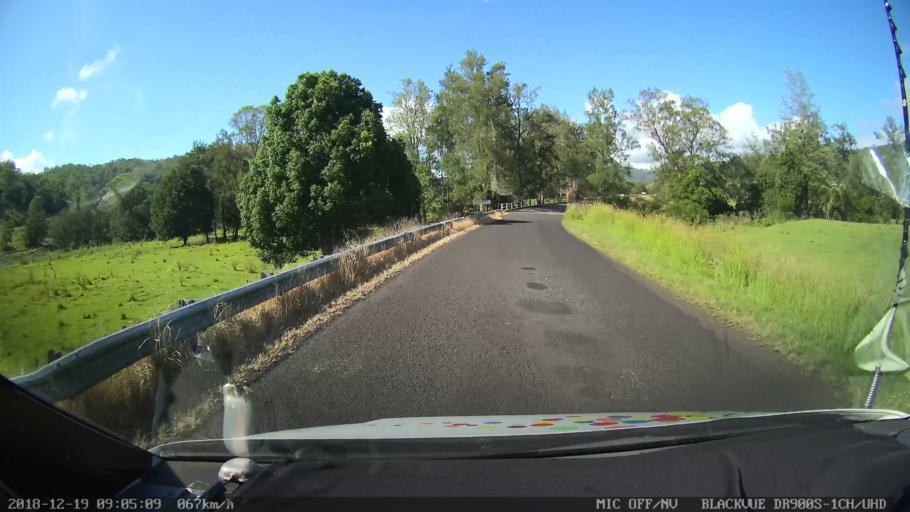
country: AU
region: New South Wales
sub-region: Kyogle
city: Kyogle
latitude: -28.4621
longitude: 152.9454
